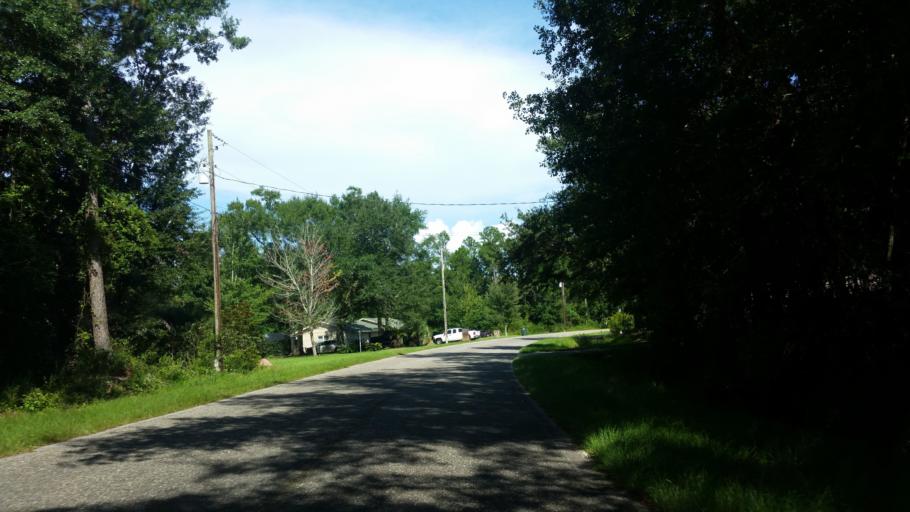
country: US
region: Florida
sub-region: Santa Rosa County
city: Pace
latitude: 30.5816
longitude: -87.1556
